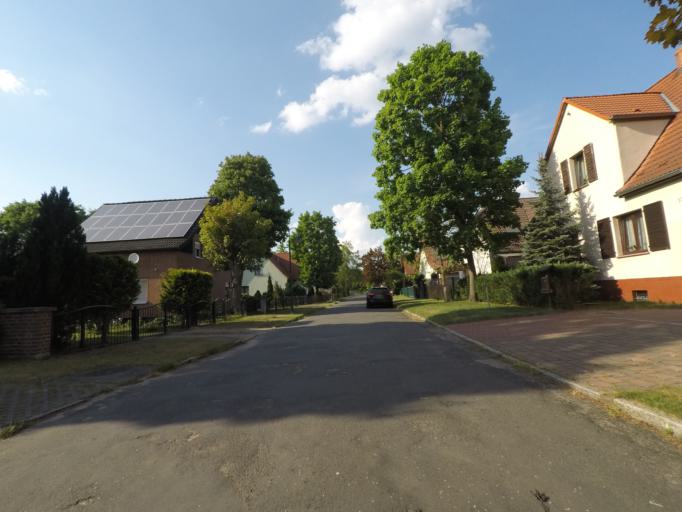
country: DE
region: Brandenburg
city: Melchow
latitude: 52.8374
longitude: 13.7230
